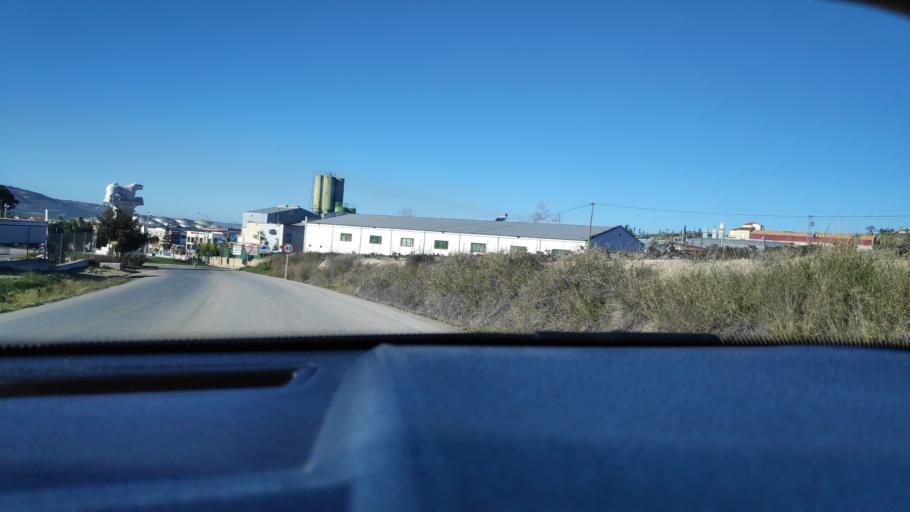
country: ES
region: Andalusia
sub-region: Province of Cordoba
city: Baena
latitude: 37.6231
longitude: -4.3071
